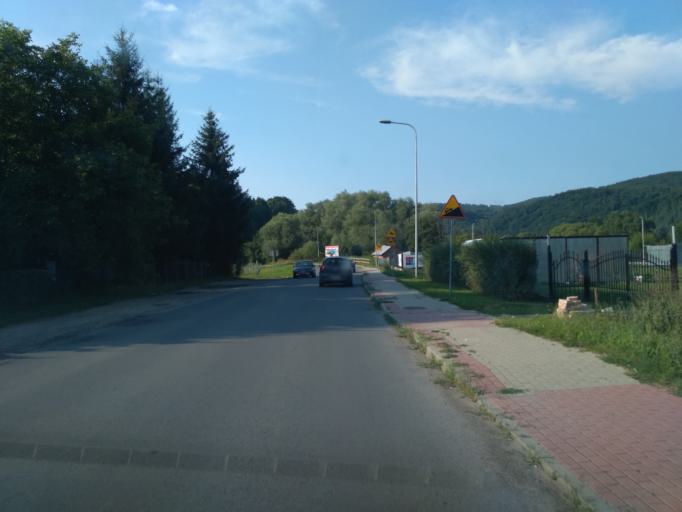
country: PL
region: Subcarpathian Voivodeship
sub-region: Powiat sanocki
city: Sanok
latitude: 49.5770
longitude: 22.1959
